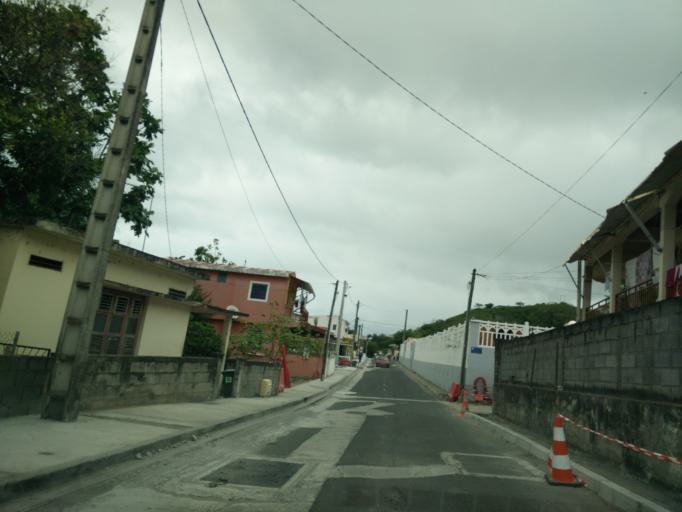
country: MQ
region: Martinique
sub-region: Martinique
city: Saint-Pierre
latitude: 14.7943
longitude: -61.2203
